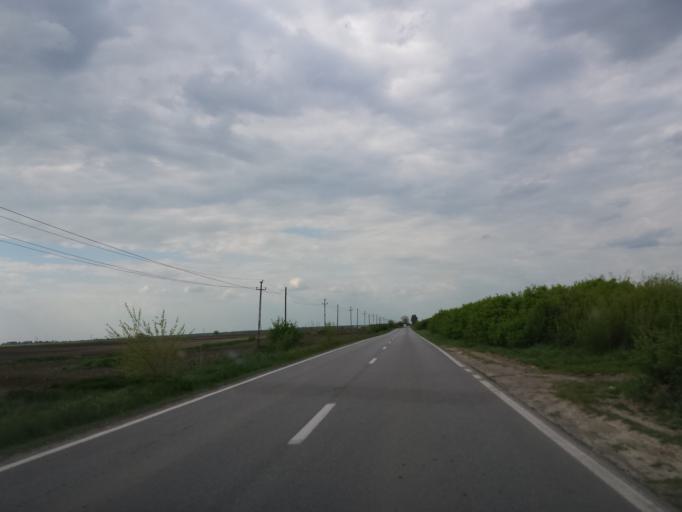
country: RO
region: Timis
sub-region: Oras Sannicolau Mare
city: Sannicolau Mare
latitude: 46.0984
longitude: 20.6002
